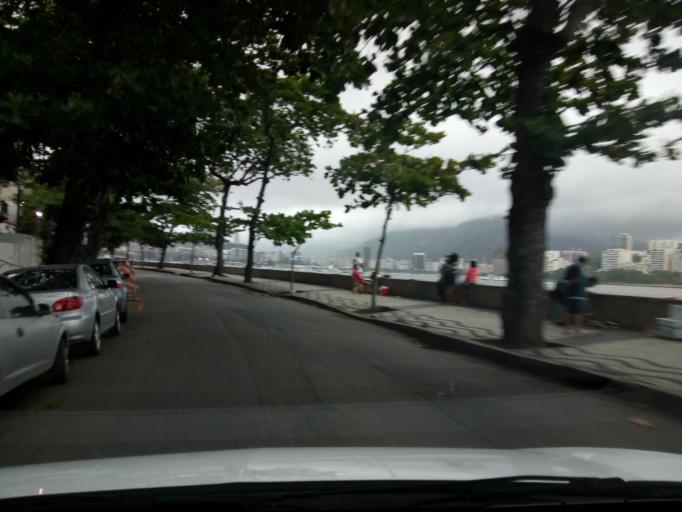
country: BR
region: Rio de Janeiro
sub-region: Rio De Janeiro
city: Rio de Janeiro
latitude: -22.9435
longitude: -43.1616
